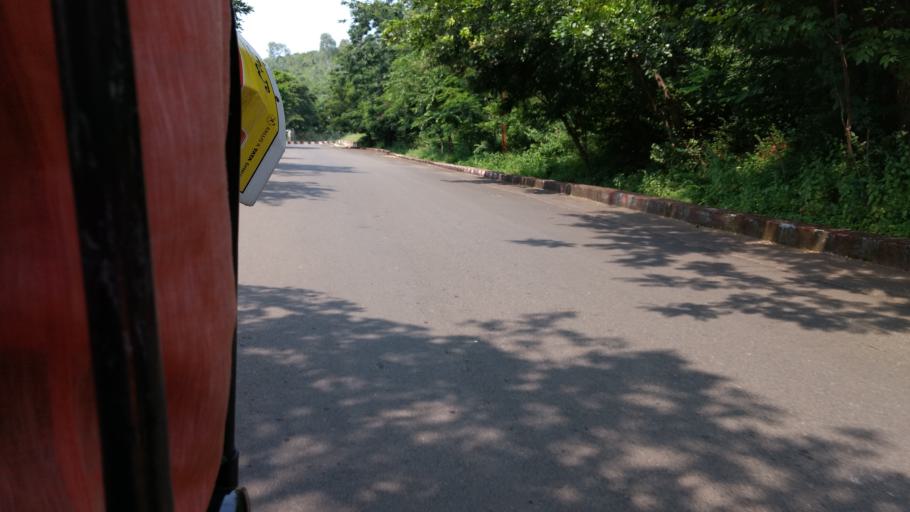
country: IN
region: Andhra Pradesh
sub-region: East Godavari
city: Tuni
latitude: 17.2795
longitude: 82.3990
